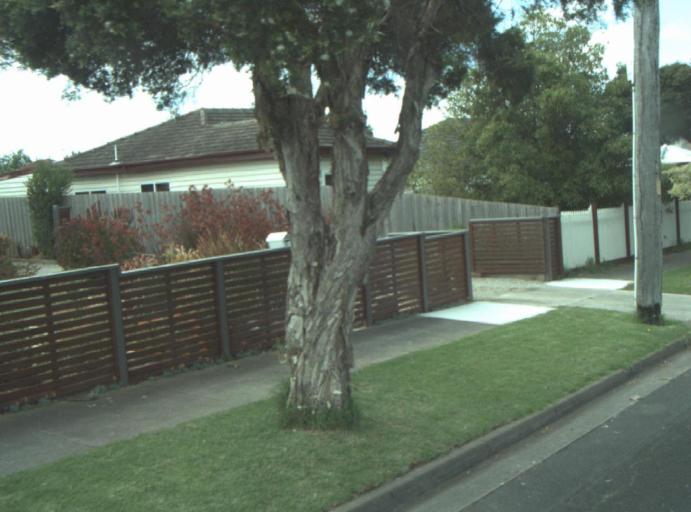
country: AU
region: Victoria
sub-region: Greater Geelong
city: Wandana Heights
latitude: -38.1823
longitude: 144.3317
